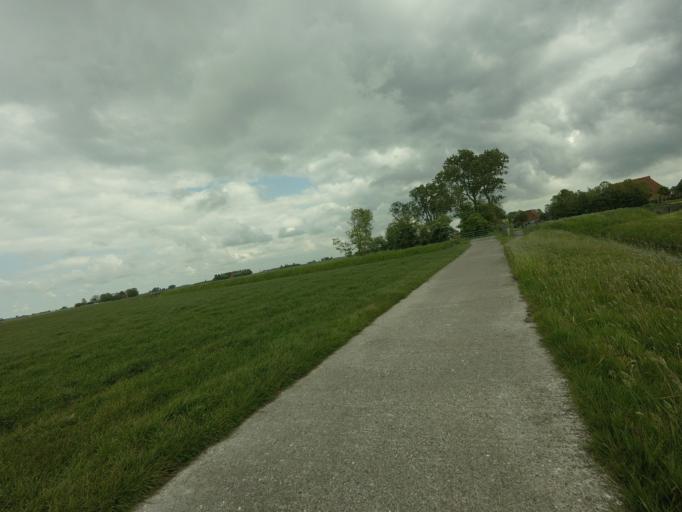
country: NL
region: Friesland
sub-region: Gemeente Littenseradiel
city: Wommels
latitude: 53.1101
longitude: 5.6105
